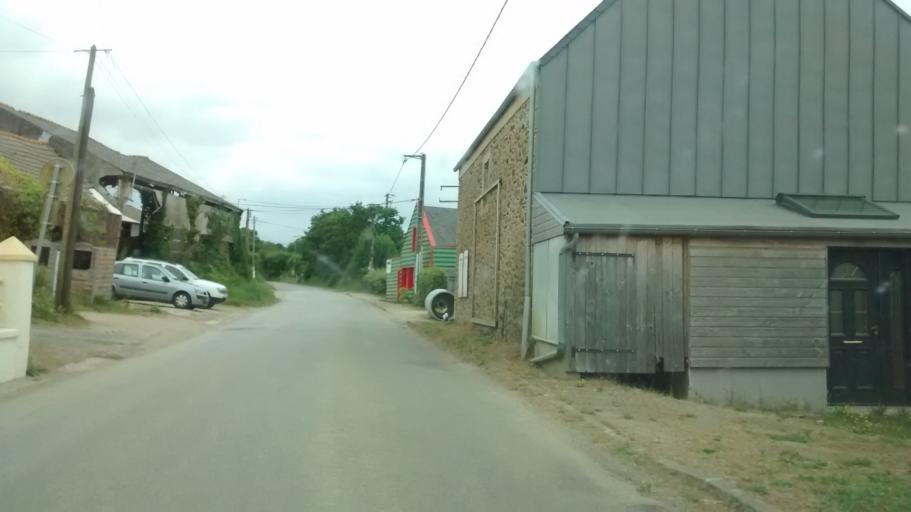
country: FR
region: Brittany
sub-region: Departement du Finistere
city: Plougastel-Daoulas
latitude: 48.3555
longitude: -4.3885
